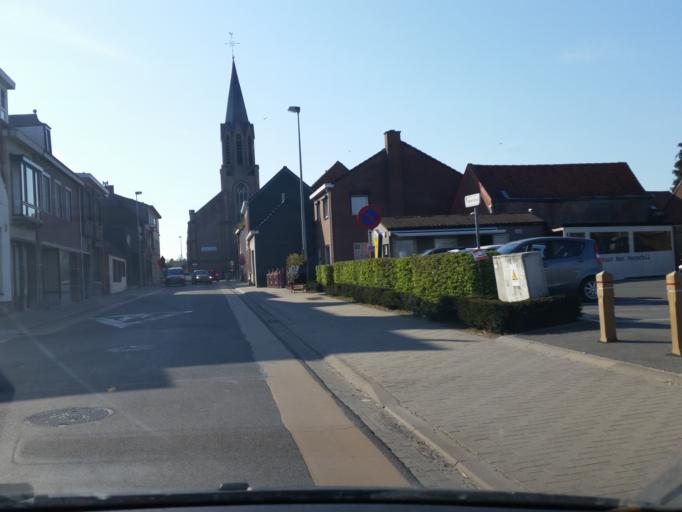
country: NL
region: Zeeland
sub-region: Gemeente Hulst
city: Hulst
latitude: 51.2558
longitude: 4.0914
